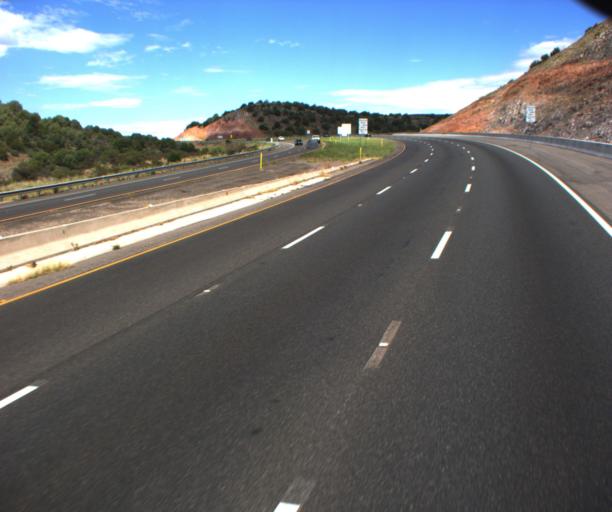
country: US
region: Arizona
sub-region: Yavapai County
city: Camp Verde
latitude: 34.5331
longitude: -111.9569
